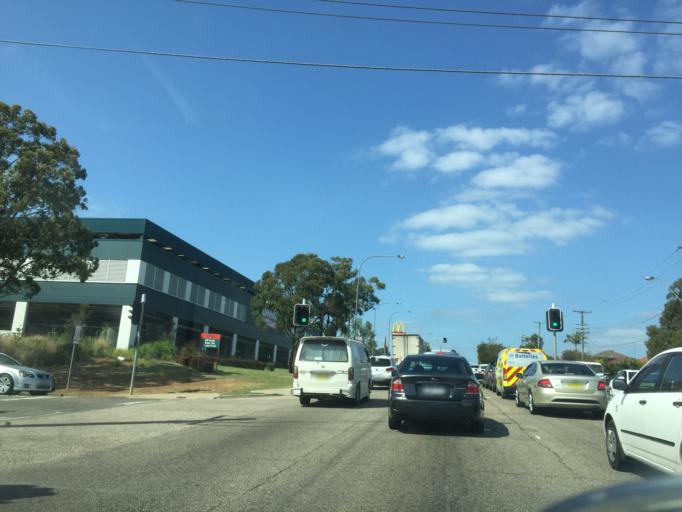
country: AU
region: New South Wales
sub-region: Canterbury
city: Belfield
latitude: -33.9004
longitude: 151.0652
